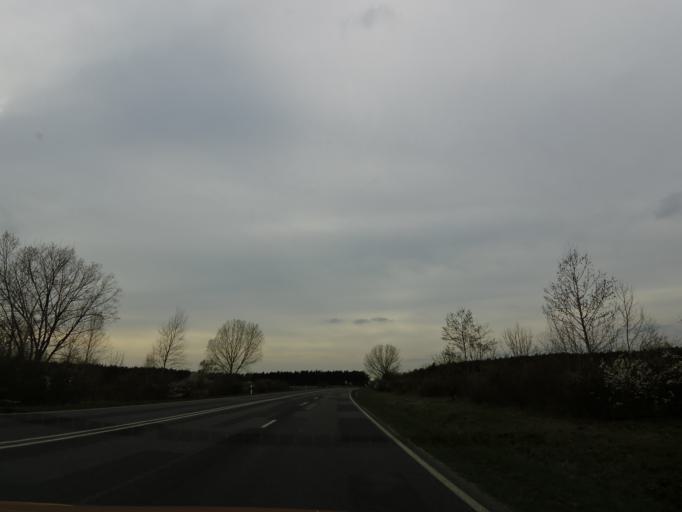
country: DE
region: Brandenburg
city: Beeskow
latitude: 52.1908
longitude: 14.2819
